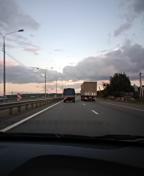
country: RU
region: Moskovskaya
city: Zhukovskiy
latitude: 55.5187
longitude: 38.1254
